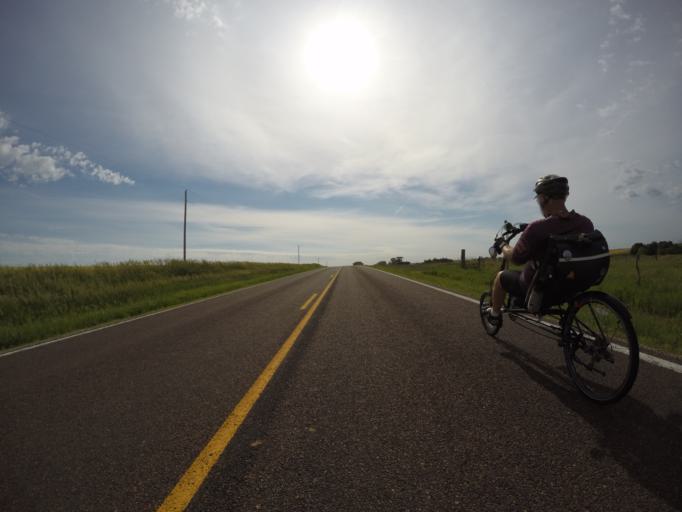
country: US
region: Kansas
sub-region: Washington County
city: Washington
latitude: 39.7124
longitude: -97.2804
